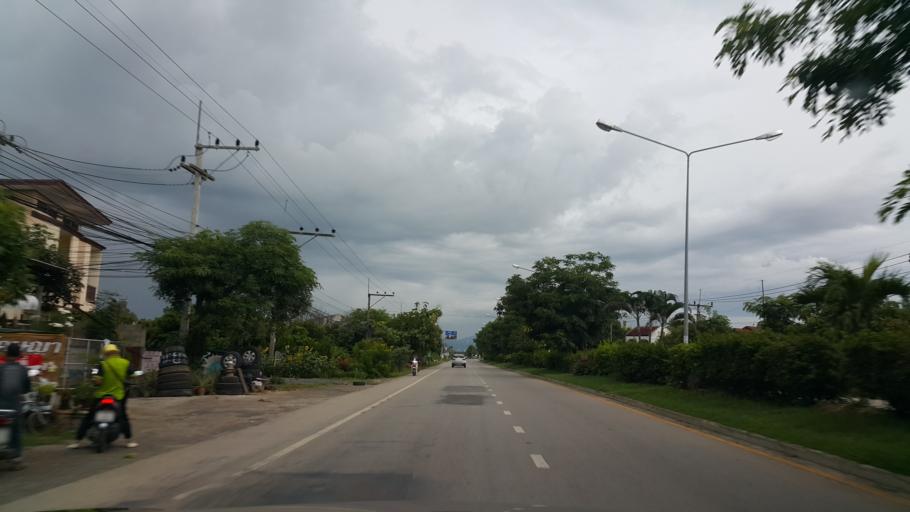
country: TH
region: Phayao
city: Dok Kham Tai
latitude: 19.1668
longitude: 100.0020
